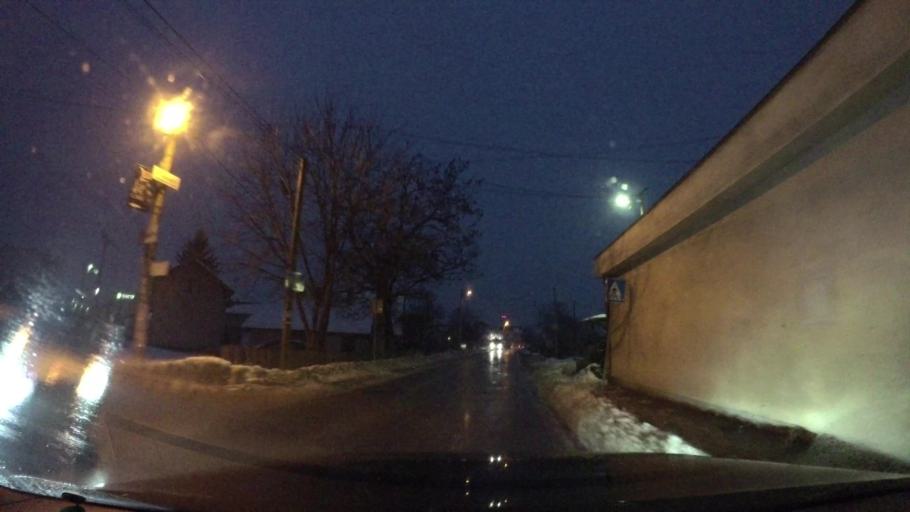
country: BA
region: Federation of Bosnia and Herzegovina
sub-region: Kanton Sarajevo
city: Sarajevo
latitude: 43.8439
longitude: 18.3220
